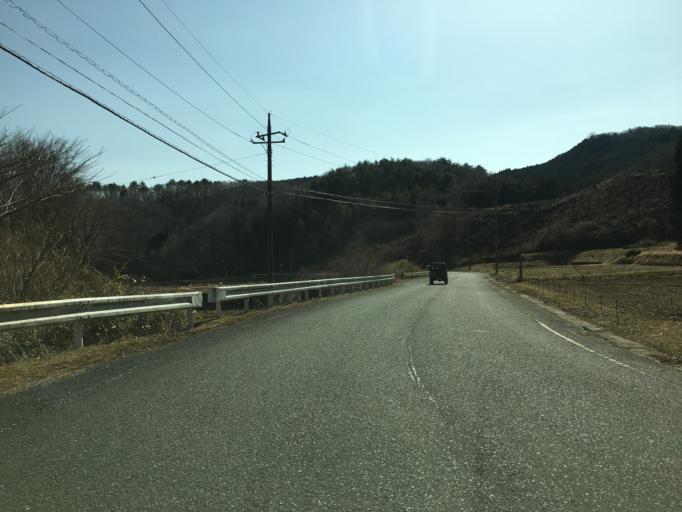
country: JP
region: Ibaraki
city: Takahagi
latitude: 36.8237
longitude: 140.5737
